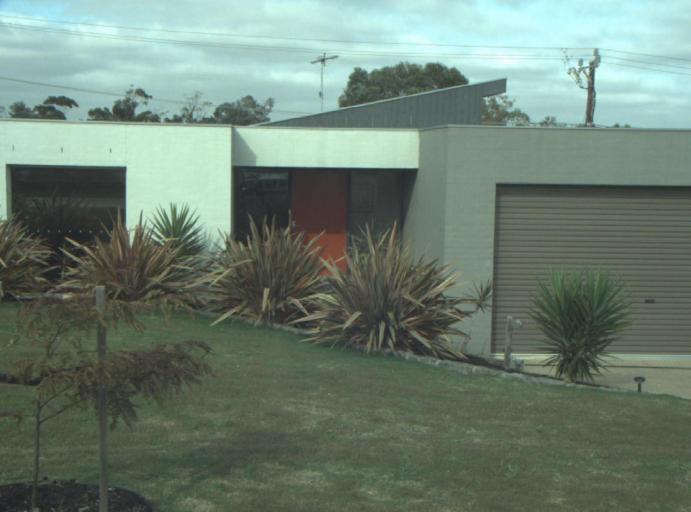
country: AU
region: Victoria
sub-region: Greater Geelong
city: Wandana Heights
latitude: -38.1554
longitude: 144.3118
